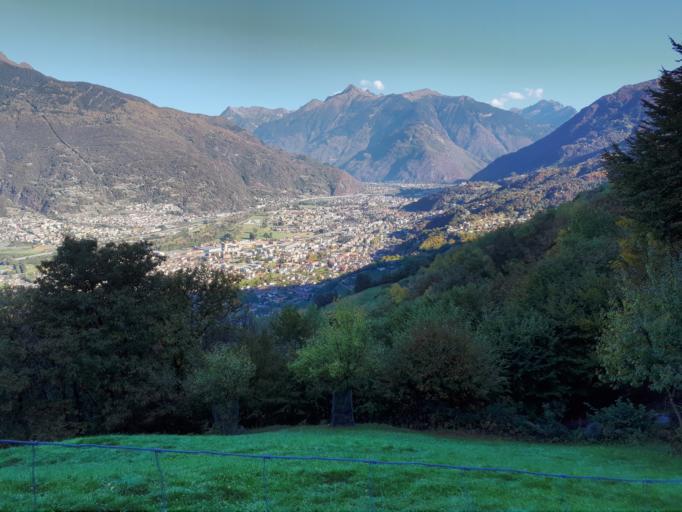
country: CH
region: Ticino
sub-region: Bellinzona District
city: Camorino
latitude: 46.1519
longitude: 9.0059
